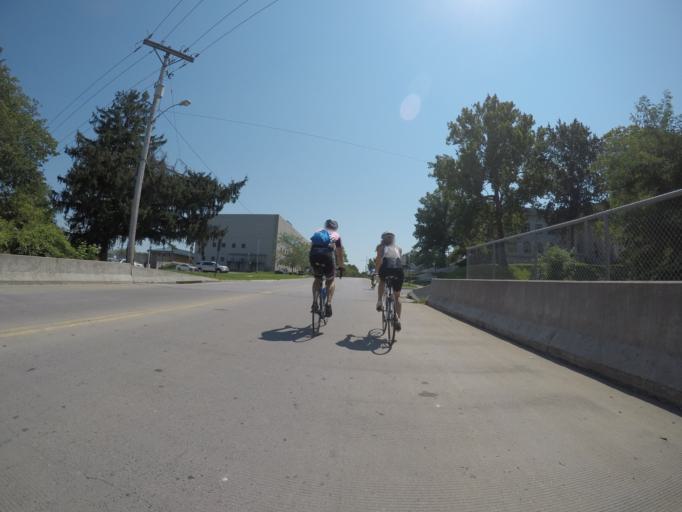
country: US
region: Kansas
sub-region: Leavenworth County
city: Leavenworth
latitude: 39.3155
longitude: -94.9117
